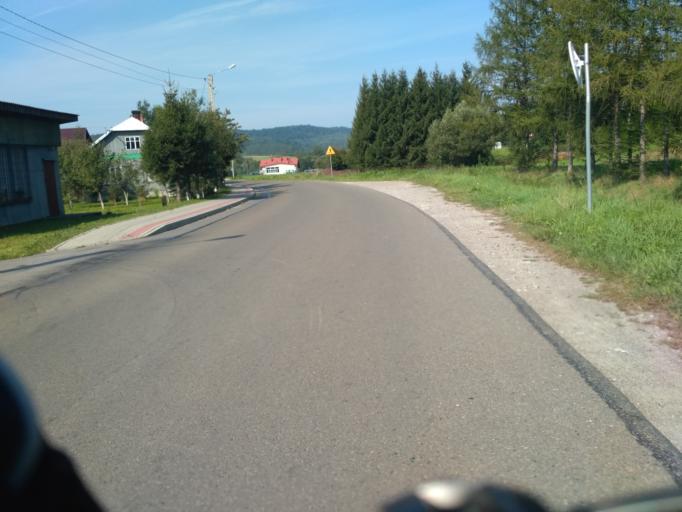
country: PL
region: Subcarpathian Voivodeship
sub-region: Powiat brzozowski
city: Golcowa
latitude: 49.7746
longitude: 22.0149
